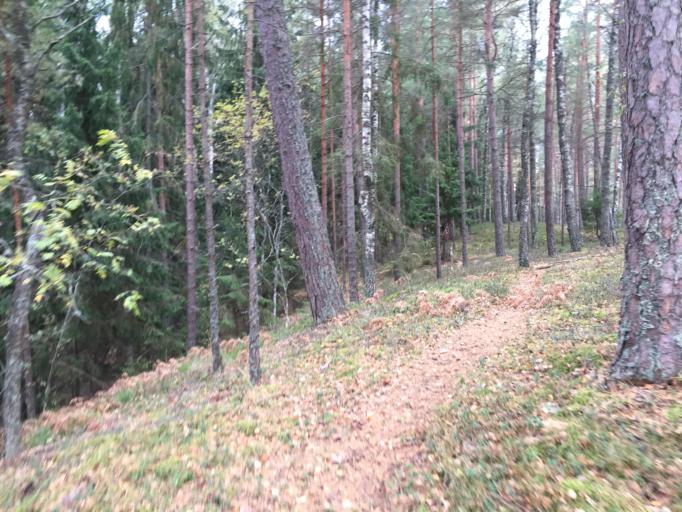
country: LV
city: Tireli
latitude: 56.8915
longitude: 23.5332
